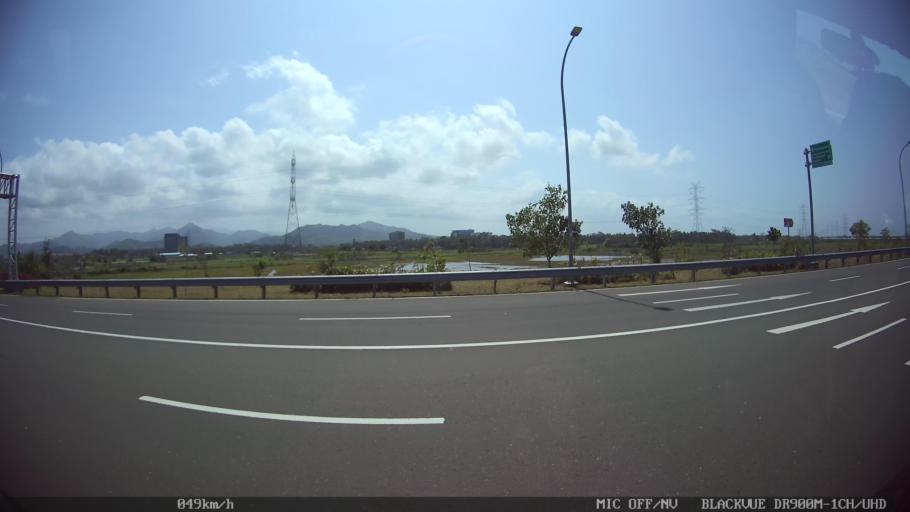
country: ID
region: Daerah Istimewa Yogyakarta
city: Srandakan
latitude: -7.8932
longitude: 110.0634
